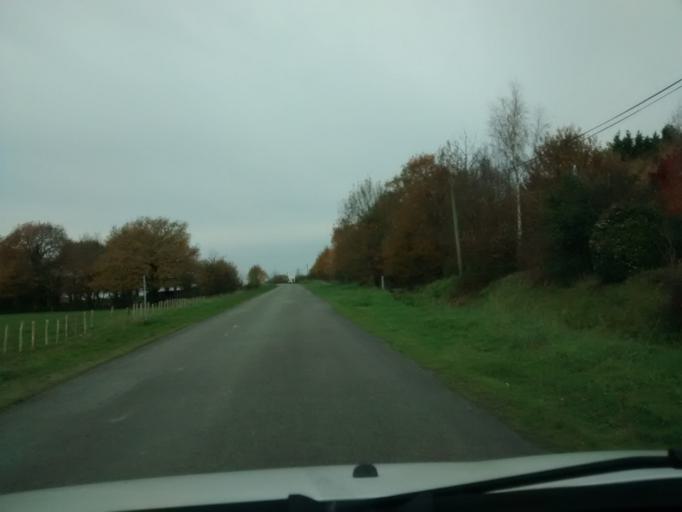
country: FR
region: Brittany
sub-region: Departement d'Ille-et-Vilaine
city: Noyal-sur-Vilaine
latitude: 48.1101
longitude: -1.5408
